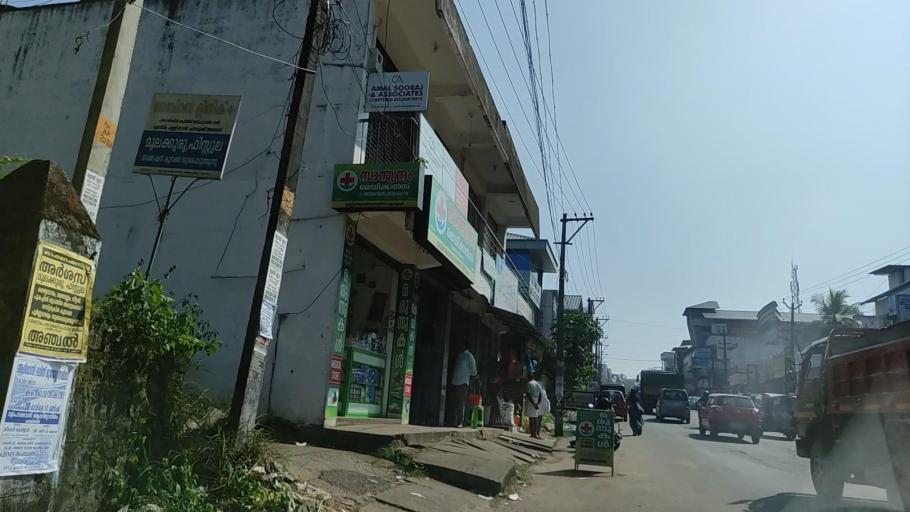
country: IN
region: Kerala
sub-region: Kollam
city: Punalur
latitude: 8.9286
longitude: 76.9100
